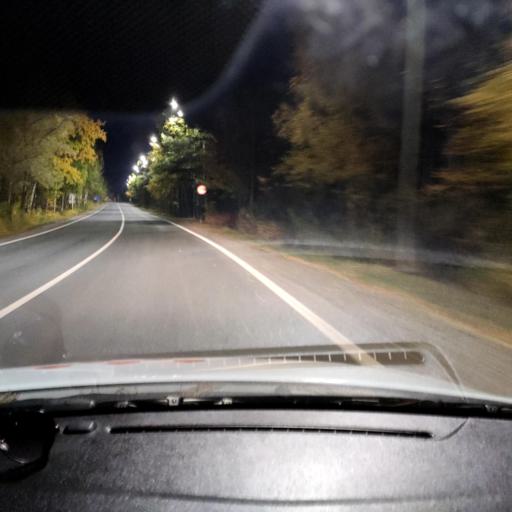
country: RU
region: Tatarstan
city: Verkhniy Uslon
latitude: 55.6369
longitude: 49.0221
